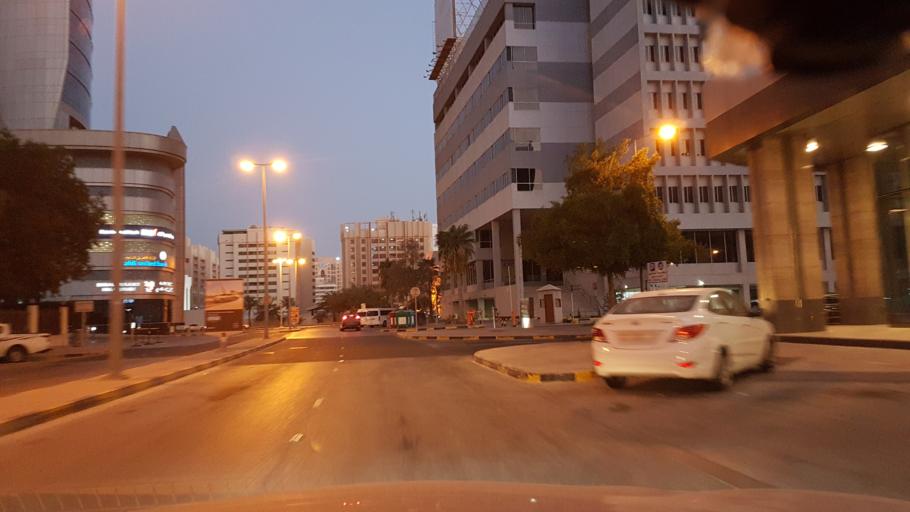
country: BH
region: Muharraq
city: Al Muharraq
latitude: 26.2416
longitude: 50.5907
